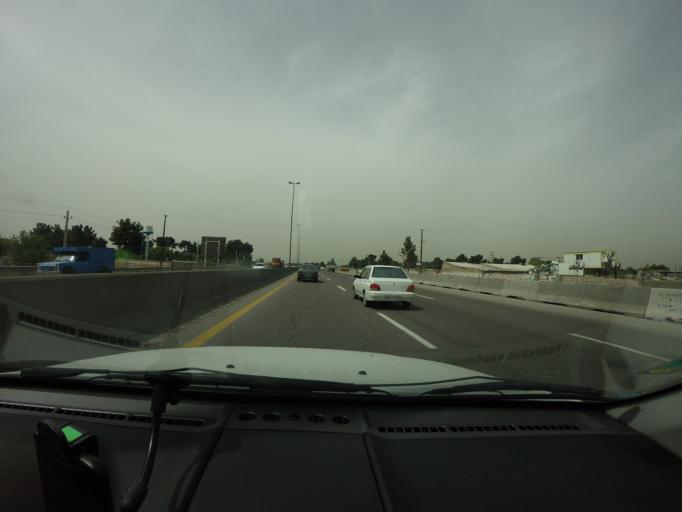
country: IR
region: Tehran
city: Eslamshahr
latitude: 35.5738
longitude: 51.1428
